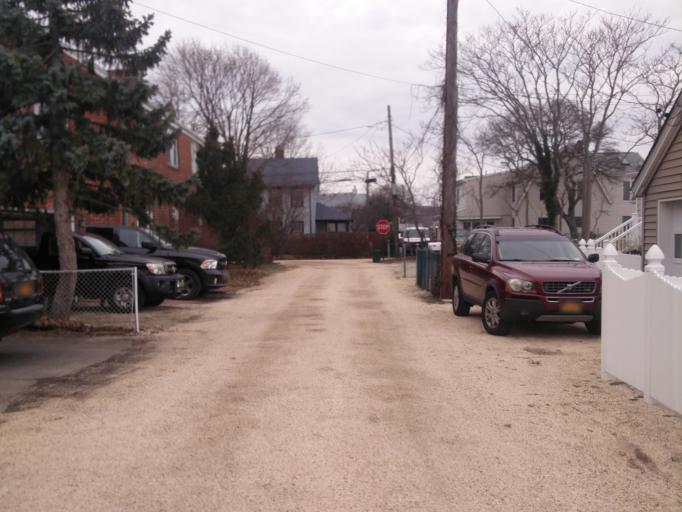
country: US
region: New York
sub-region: Nassau County
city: Bayville
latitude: 40.9082
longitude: -73.5473
